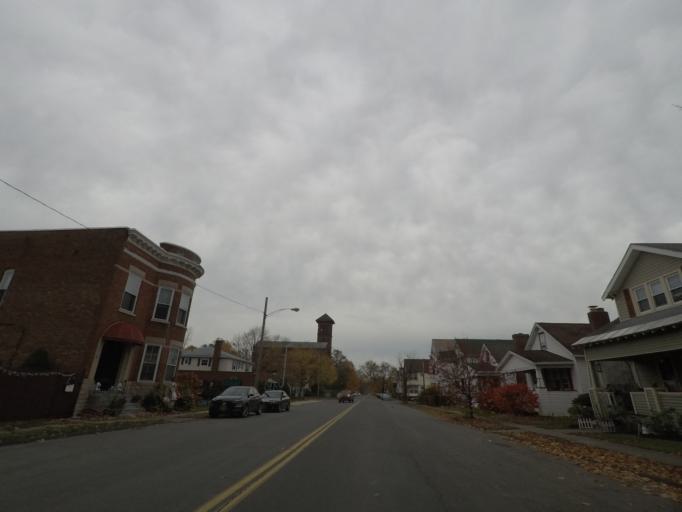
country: US
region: New York
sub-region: Albany County
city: Cohoes
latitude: 42.7664
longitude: -73.6797
